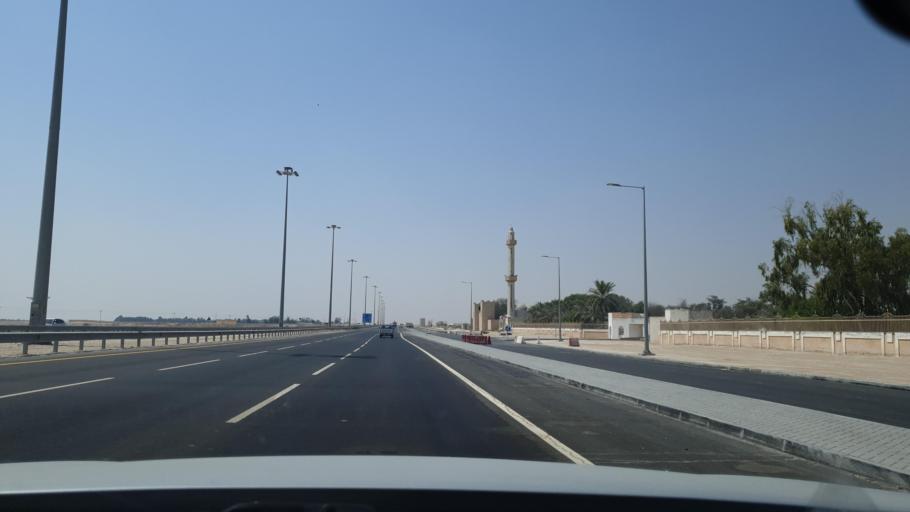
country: QA
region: Al Khawr
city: Al Khawr
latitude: 25.6487
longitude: 51.4471
